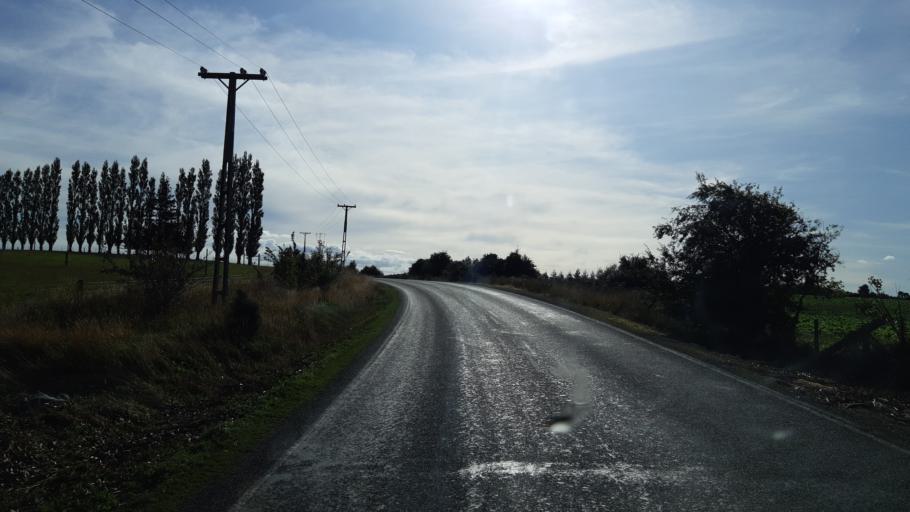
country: NZ
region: Southland
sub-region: Gore District
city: Gore
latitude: -46.1099
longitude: 168.8678
